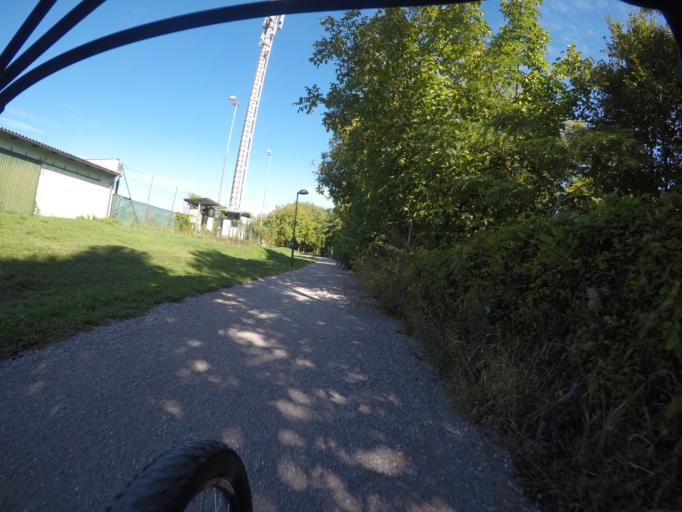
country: AT
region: Lower Austria
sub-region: Politischer Bezirk Modling
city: Brunn am Gebirge
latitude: 48.1033
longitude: 16.2990
